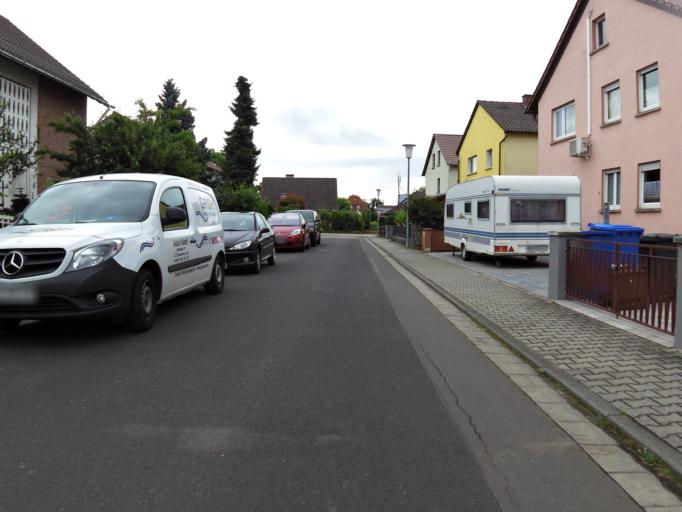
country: DE
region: Rheinland-Pfalz
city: Dirmstein
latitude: 49.5687
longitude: 8.2467
